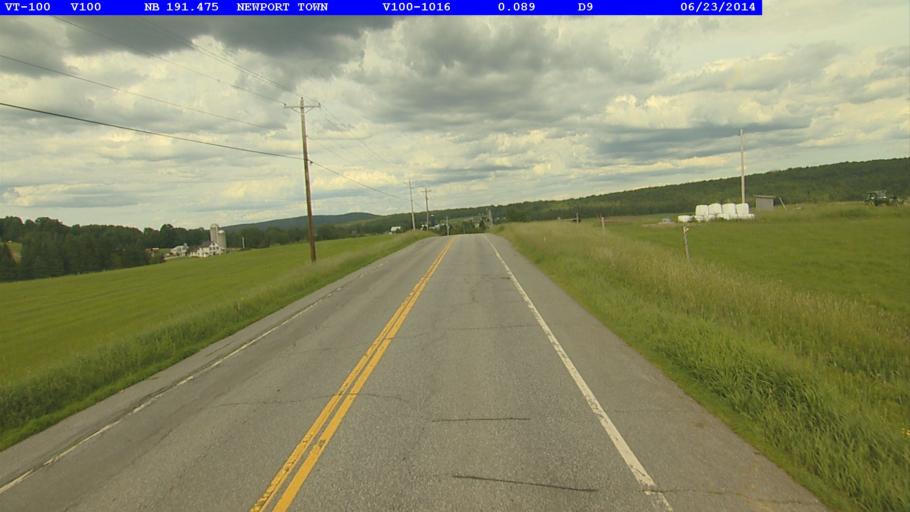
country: US
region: Vermont
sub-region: Orleans County
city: Newport
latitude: 44.9145
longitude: -72.3511
